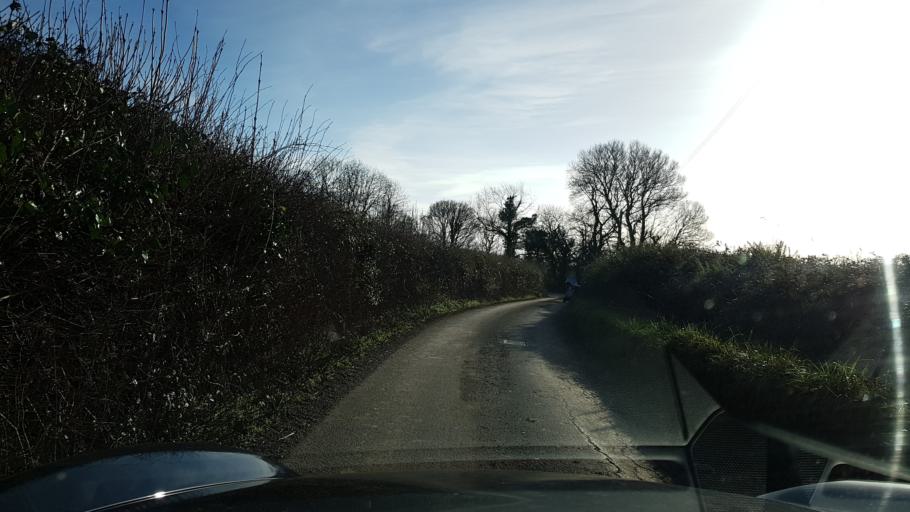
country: GB
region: England
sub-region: Dorset
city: Lyme Regis
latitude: 50.7880
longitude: -2.8693
